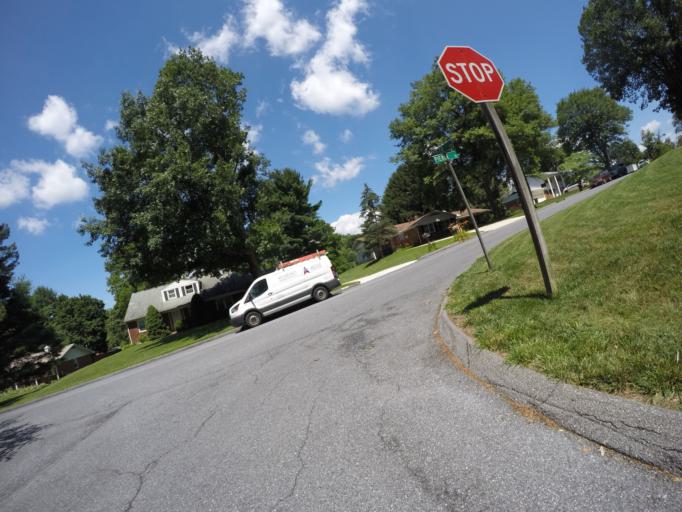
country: US
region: Maryland
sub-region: Howard County
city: Columbia
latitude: 39.2762
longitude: -76.8600
